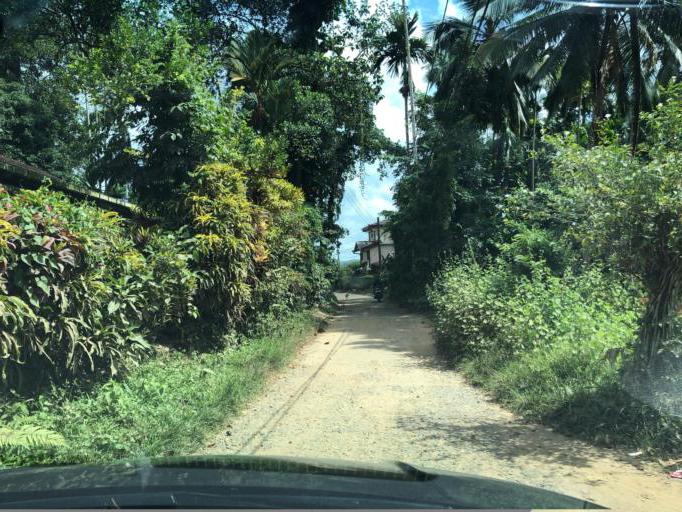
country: LK
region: Western
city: Horawala Junction
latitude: 6.5393
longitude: 80.0958
